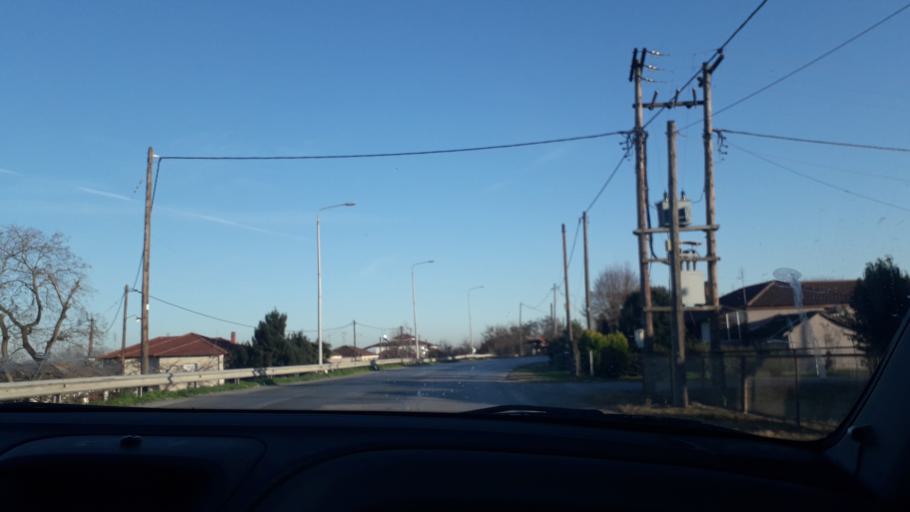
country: GR
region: Central Macedonia
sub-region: Nomos Imathias
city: Alexandreia
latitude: 40.5969
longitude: 22.4618
